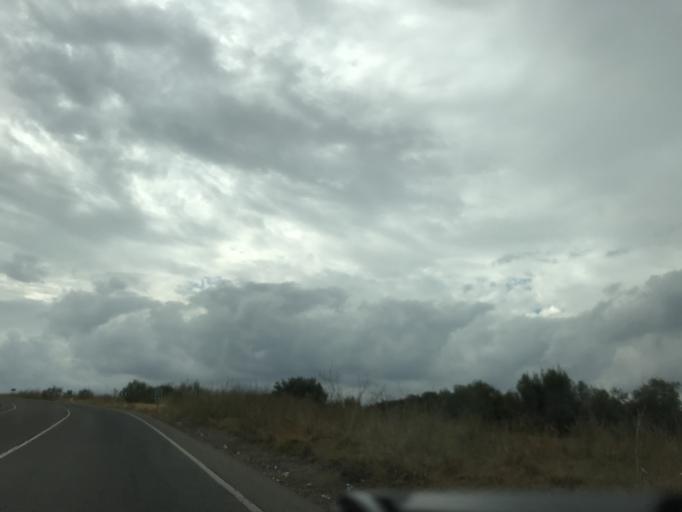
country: ES
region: Andalusia
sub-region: Provincia de Sevilla
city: Tocina
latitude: 37.6401
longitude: -5.7508
